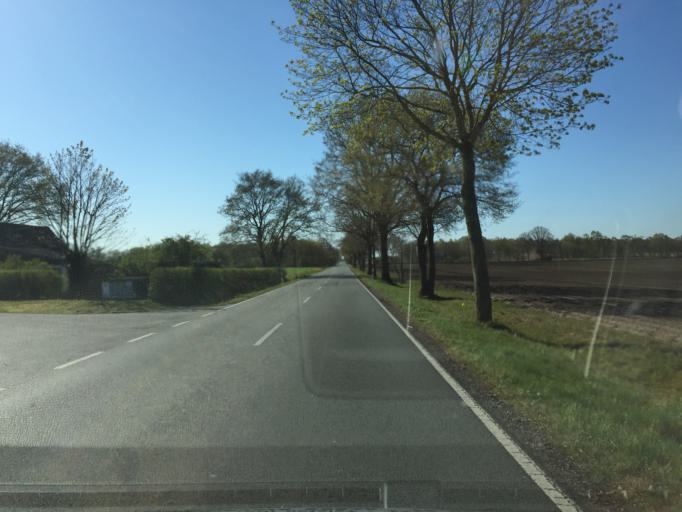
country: DE
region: Lower Saxony
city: Varrel
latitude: 52.6423
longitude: 8.7341
